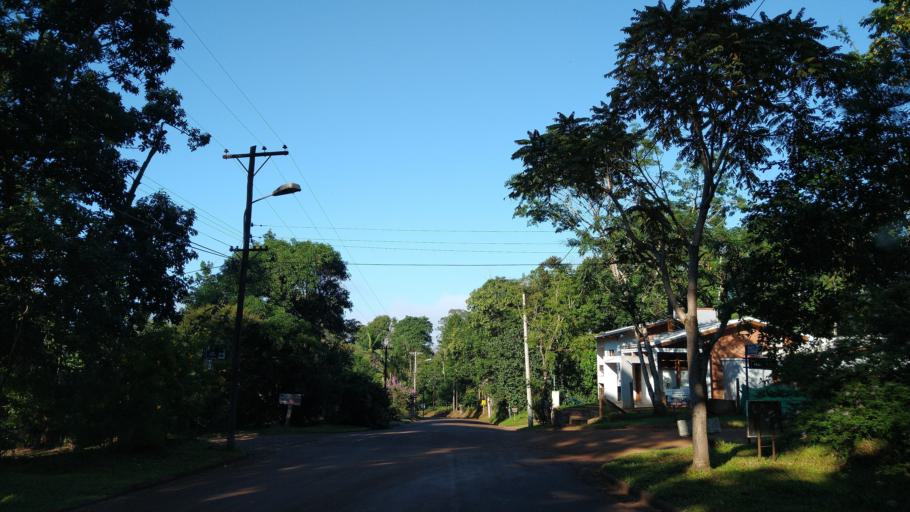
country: AR
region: Misiones
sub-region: Departamento de Montecarlo
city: Montecarlo
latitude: -26.5584
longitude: -54.7762
